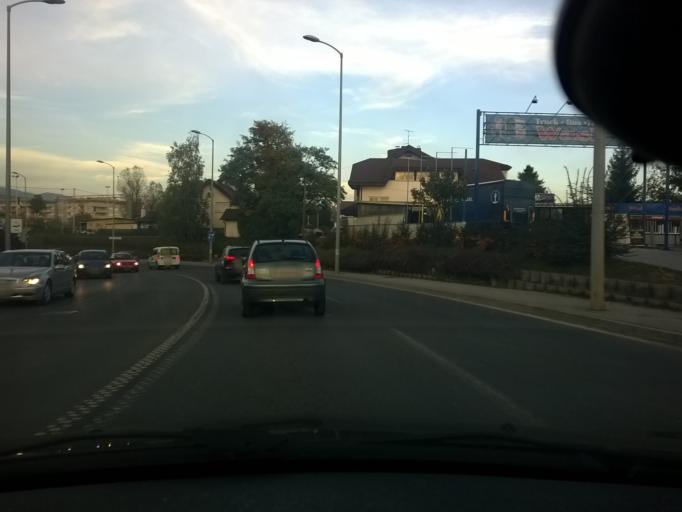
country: HR
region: Grad Zagreb
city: Stenjevec
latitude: 45.8131
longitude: 15.8628
